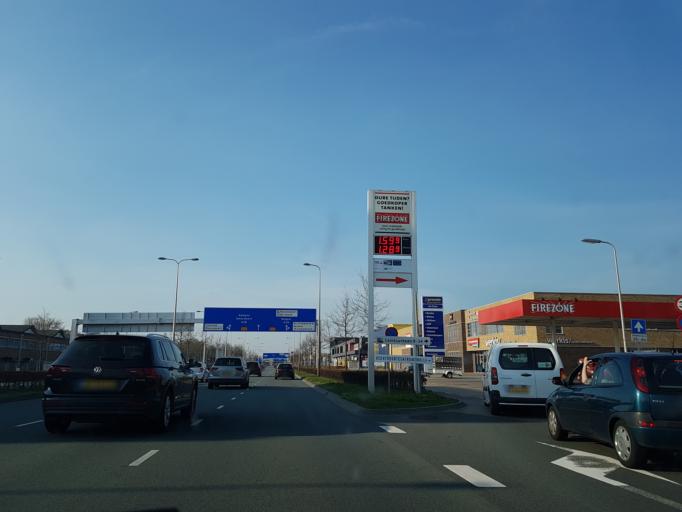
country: NL
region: Overijssel
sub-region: Gemeente Zwolle
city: Zwolle
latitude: 52.5199
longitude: 6.1184
